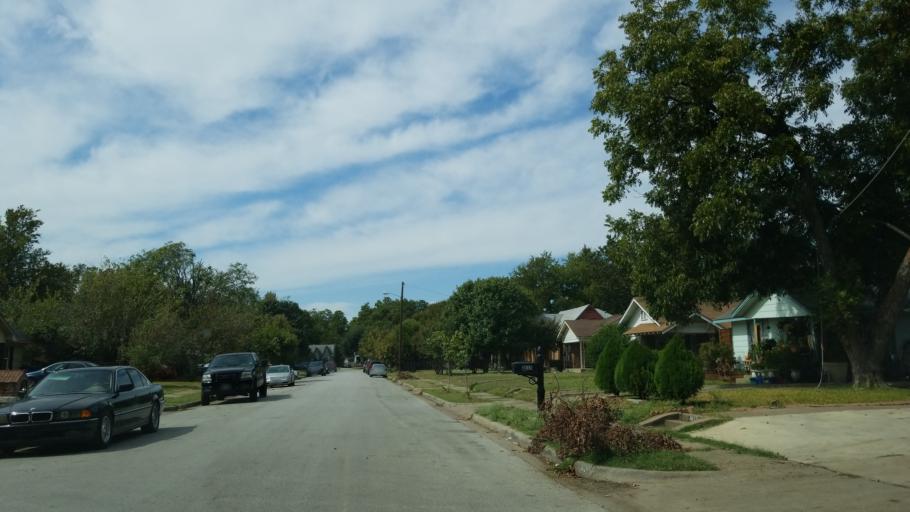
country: US
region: Texas
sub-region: Dallas County
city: Dallas
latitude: 32.7884
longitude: -96.7412
